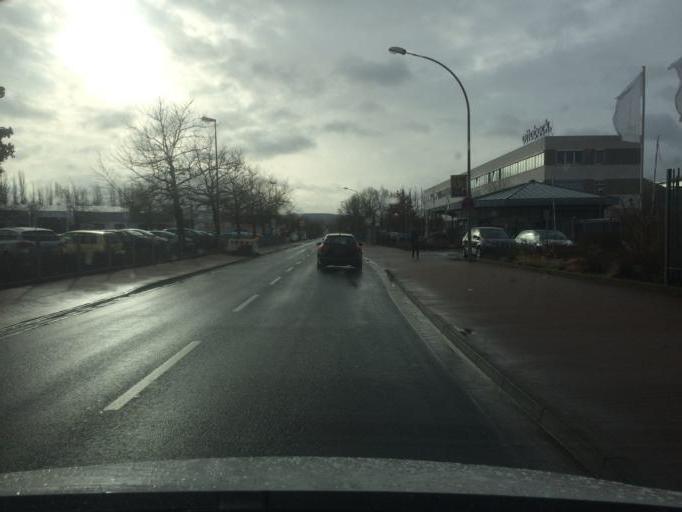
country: DE
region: Lower Saxony
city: Duderstadt
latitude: 51.5169
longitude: 10.2373
